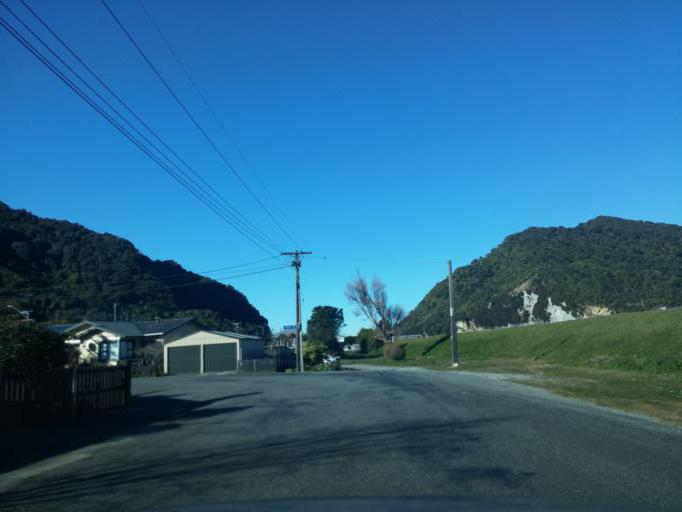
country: NZ
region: West Coast
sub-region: Grey District
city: Greymouth
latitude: -42.4433
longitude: 171.2114
